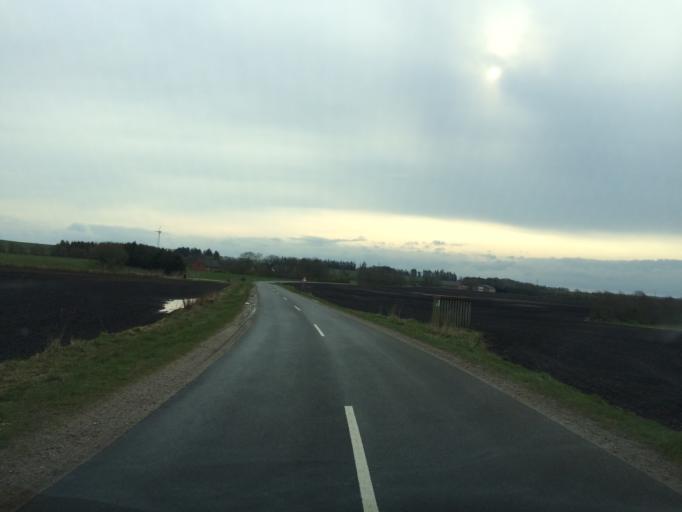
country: DK
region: Central Jutland
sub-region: Holstebro Kommune
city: Ulfborg
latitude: 56.2049
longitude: 8.4808
